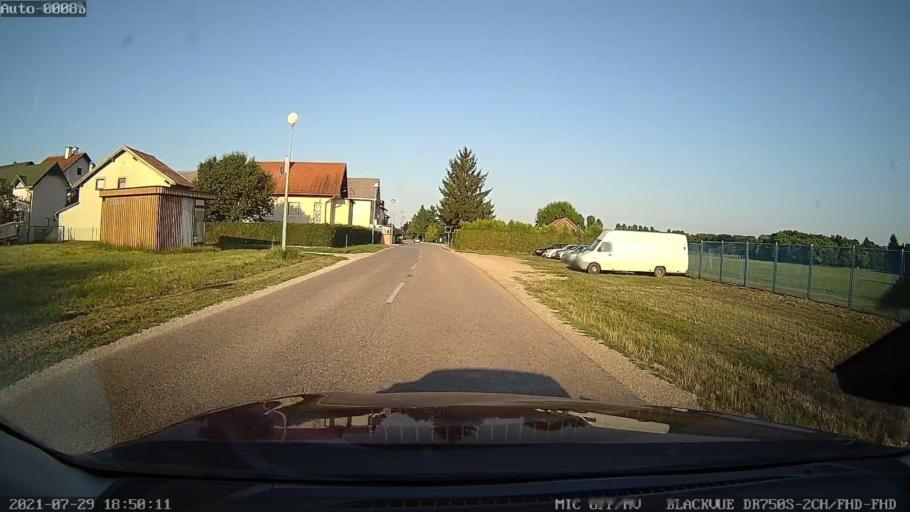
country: HR
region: Varazdinska
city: Varazdin
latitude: 46.3105
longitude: 16.3157
